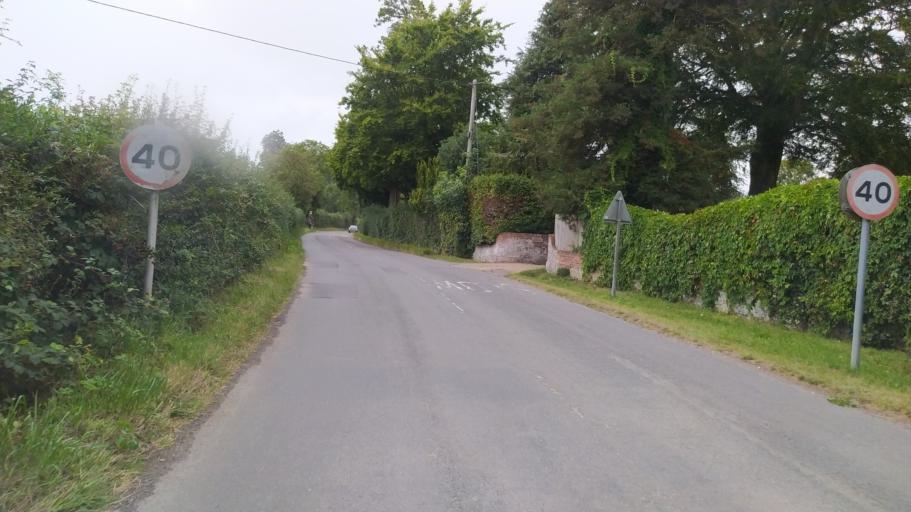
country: GB
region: England
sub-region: Hampshire
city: Four Marks
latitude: 51.0112
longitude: -1.0734
